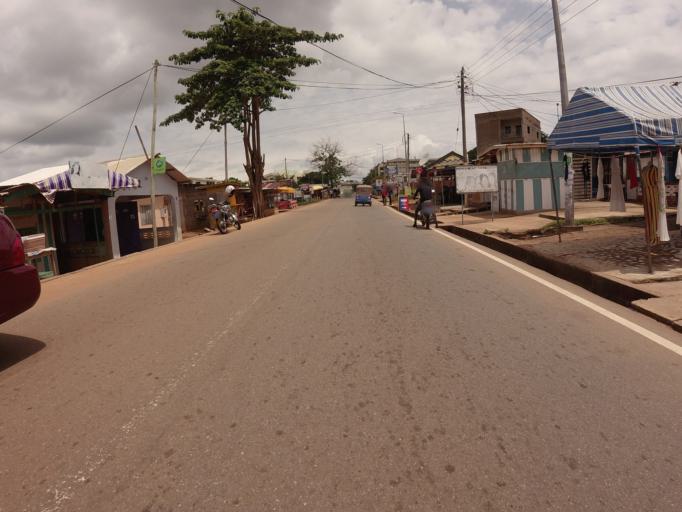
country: GH
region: Volta
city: Ho
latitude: 6.5934
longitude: 0.4710
